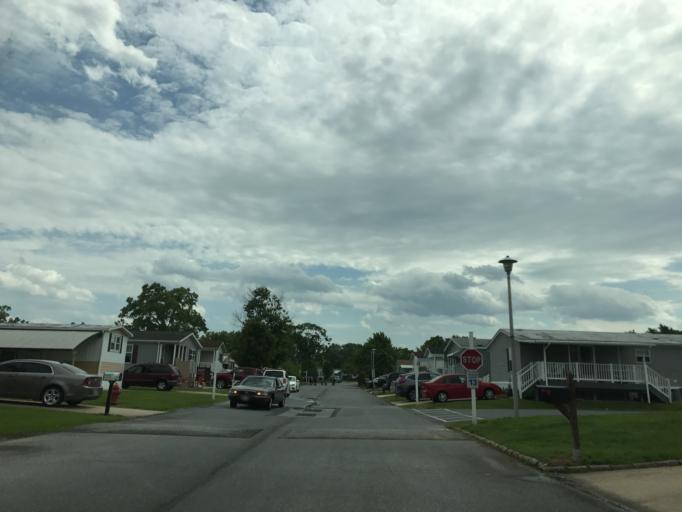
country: US
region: Maryland
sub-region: Baltimore County
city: Bowleys Quarters
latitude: 39.3417
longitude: -76.4015
